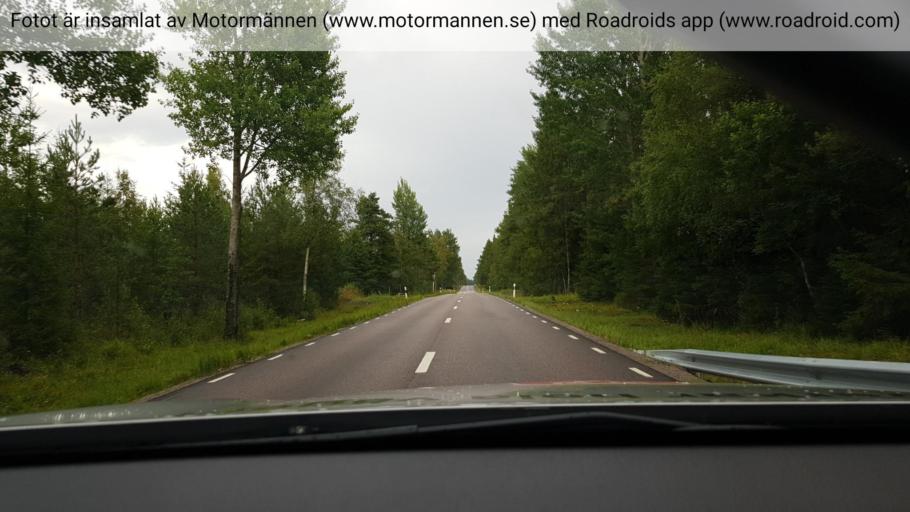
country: SE
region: Uppsala
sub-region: Osthammars Kommun
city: Gimo
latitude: 60.3650
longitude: 18.0599
